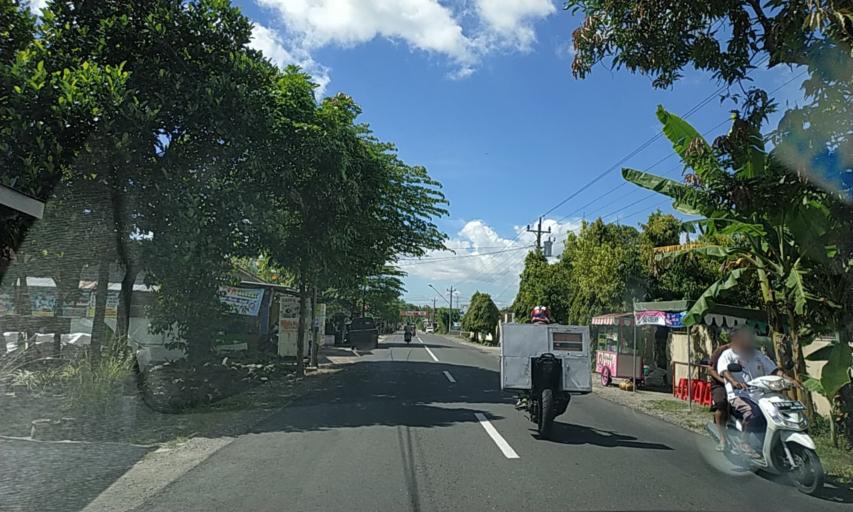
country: ID
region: Central Java
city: Trucuk
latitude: -7.7207
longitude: 110.6659
